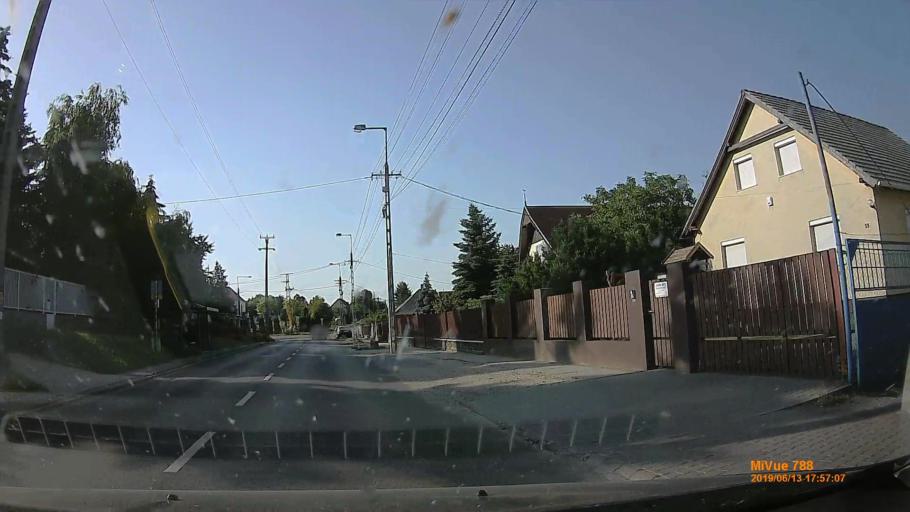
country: HU
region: Pest
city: Ecser
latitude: 47.4449
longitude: 19.3394
